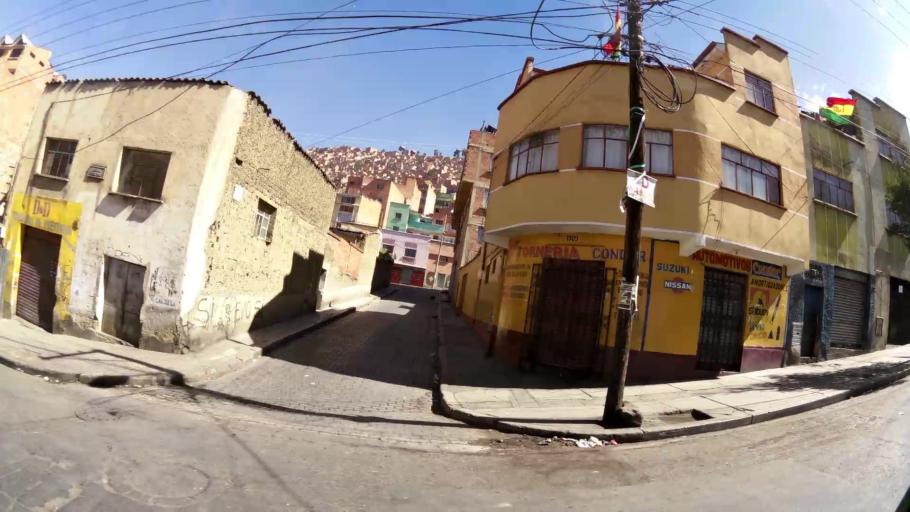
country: BO
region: La Paz
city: La Paz
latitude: -16.4961
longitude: -68.1580
